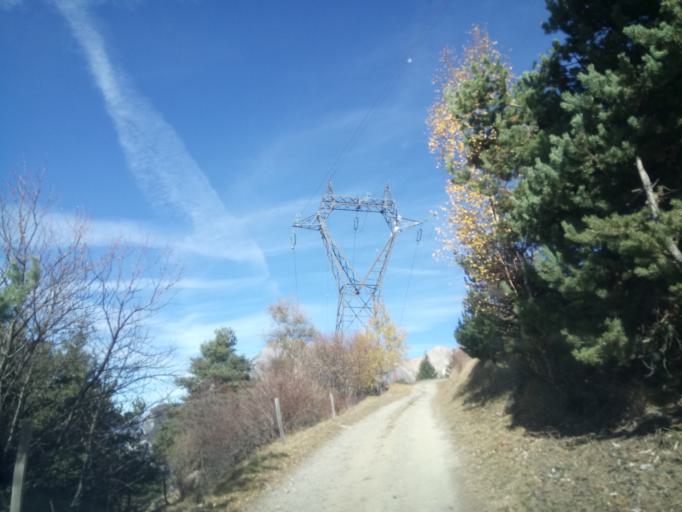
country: FR
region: Rhone-Alpes
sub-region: Departement de la Savoie
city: Saint-Michel-de-Maurienne
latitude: 45.2296
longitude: 6.4889
